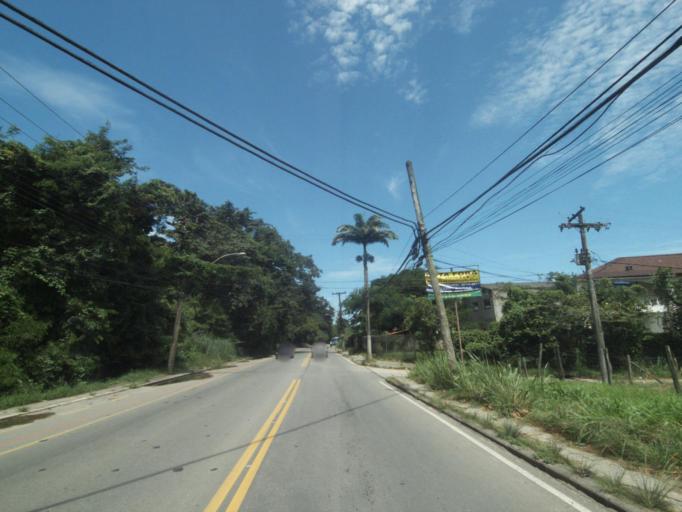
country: BR
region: Rio de Janeiro
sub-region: Niteroi
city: Niteroi
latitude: -22.9473
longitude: -43.0235
